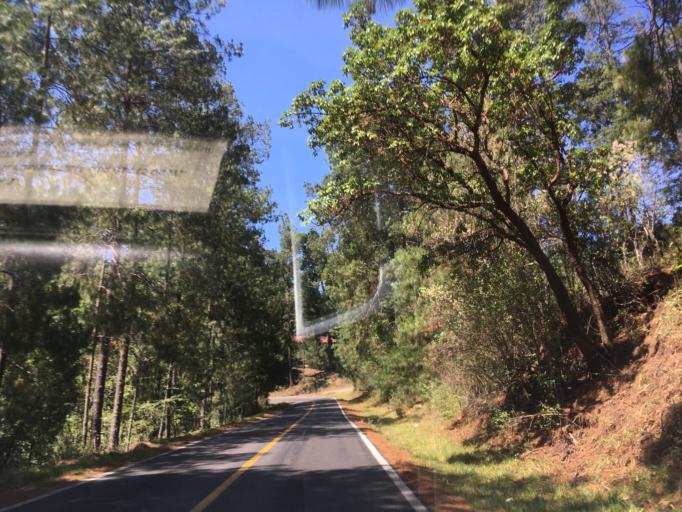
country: MX
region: Michoacan
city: Tzitzio
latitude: 19.6490
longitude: -100.7925
